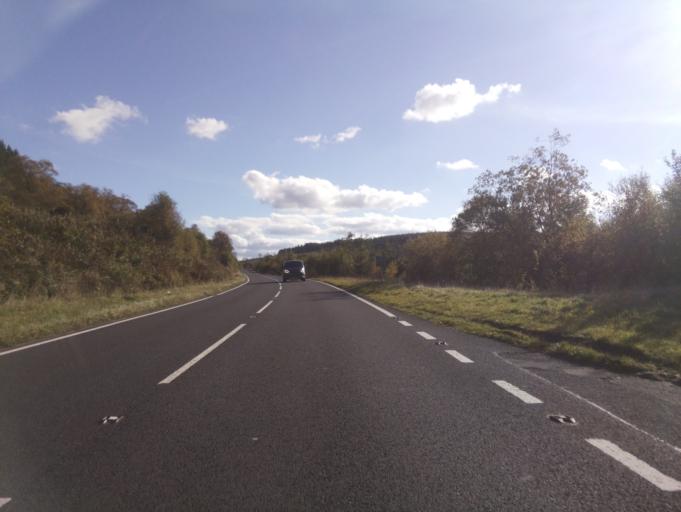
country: GB
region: Wales
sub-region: Rhondda Cynon Taf
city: Hirwaun
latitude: 51.8345
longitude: -3.4609
